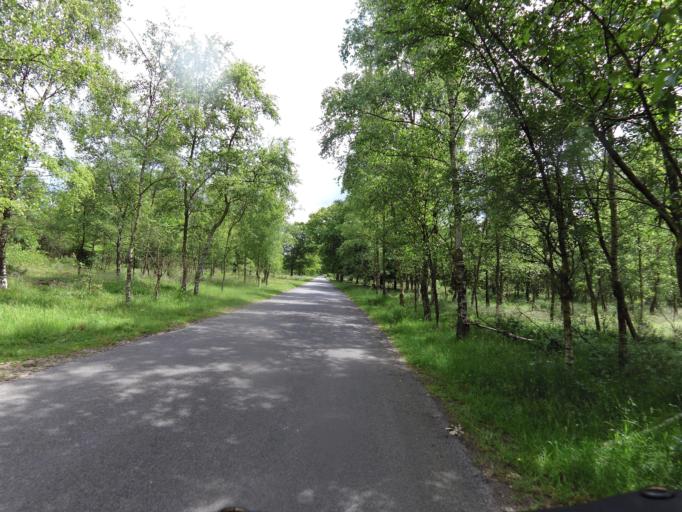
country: NL
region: Gelderland
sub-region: Gemeente Epe
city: Vaassen
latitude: 52.3091
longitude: 5.8857
